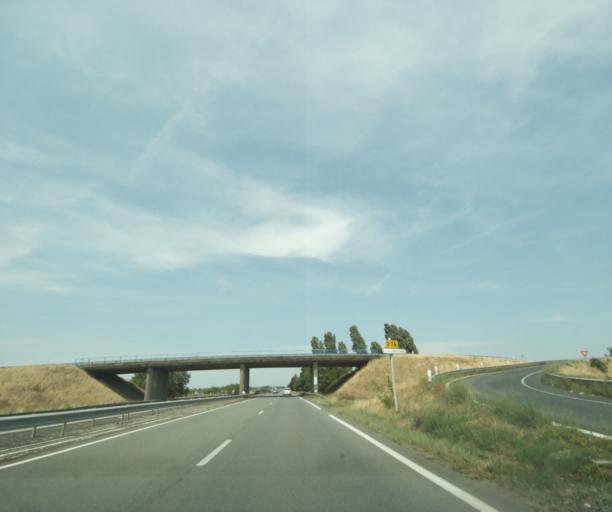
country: FR
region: Poitou-Charentes
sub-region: Departement de la Vienne
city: Dange-Saint-Romain
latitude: 46.8975
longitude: 0.5720
